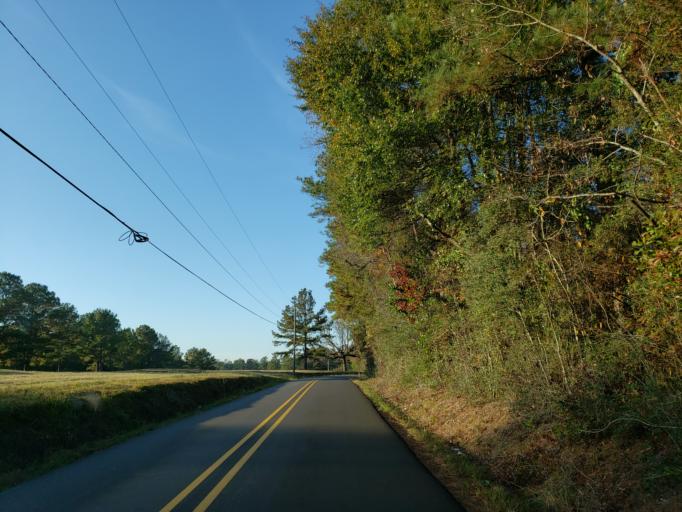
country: US
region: Mississippi
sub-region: Lamar County
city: Arnold Line
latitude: 31.3508
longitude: -89.3576
